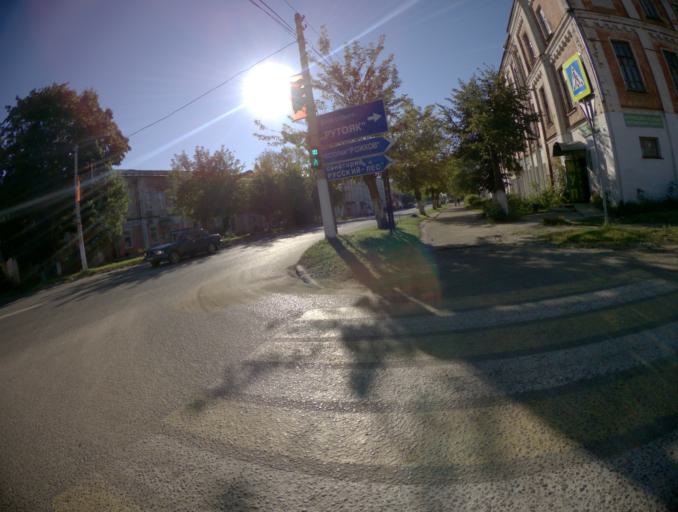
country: RU
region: Vladimir
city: Sobinka
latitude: 55.9925
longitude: 40.0188
